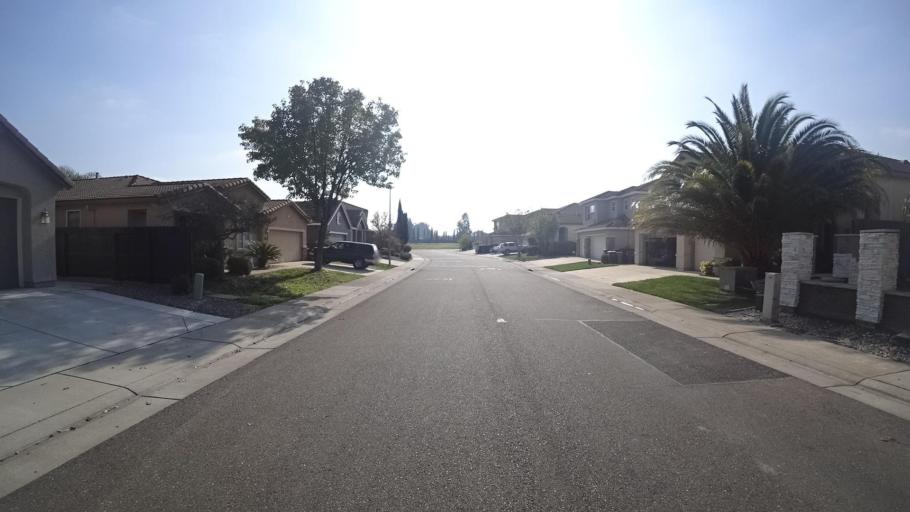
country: US
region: California
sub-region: Sacramento County
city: Vineyard
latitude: 38.4472
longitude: -121.3629
